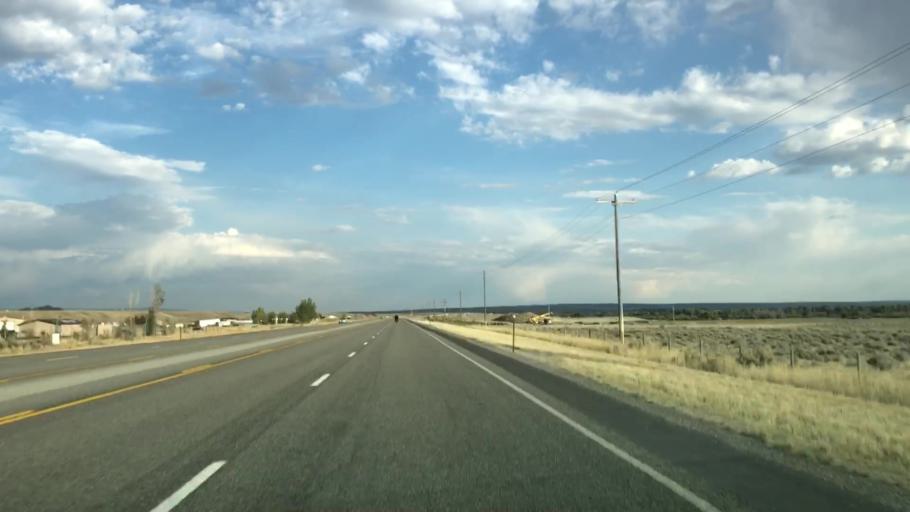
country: US
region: Wyoming
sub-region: Sublette County
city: Pinedale
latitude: 42.7752
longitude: -109.7560
